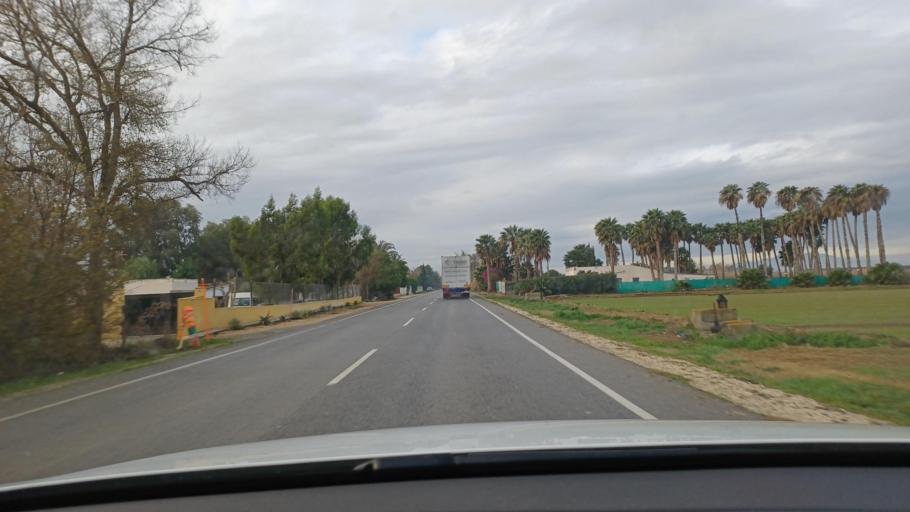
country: ES
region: Valencia
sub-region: Provincia de Alicante
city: Daya Vieja
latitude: 38.1549
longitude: -0.7095
